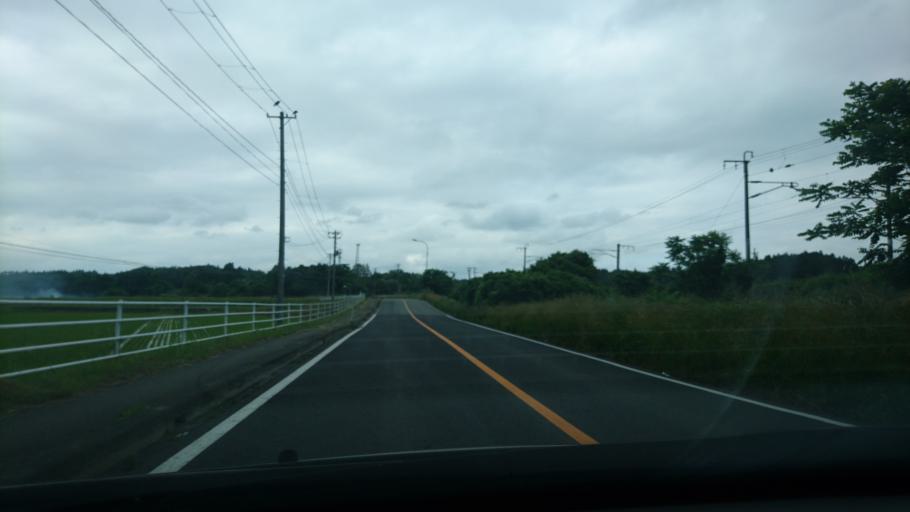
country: JP
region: Iwate
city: Ichinoseki
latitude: 38.8158
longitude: 141.1810
